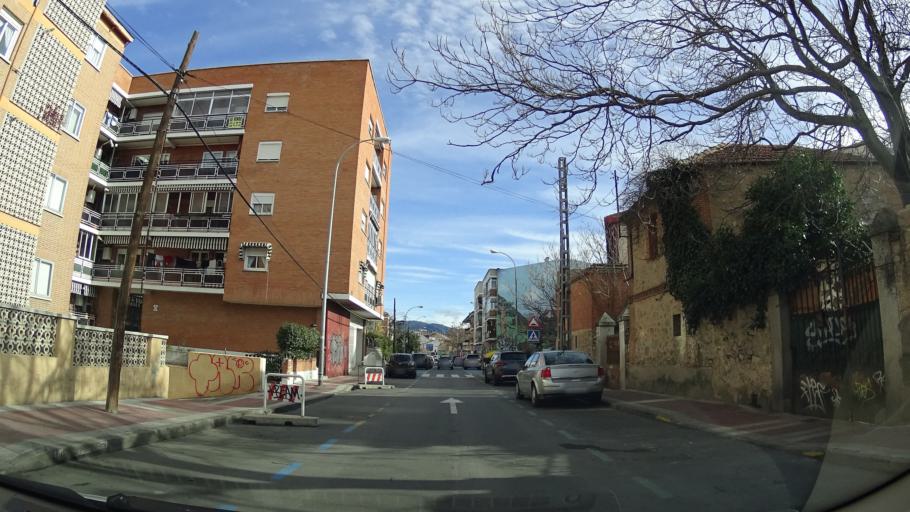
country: ES
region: Madrid
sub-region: Provincia de Madrid
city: Collado-Villalba
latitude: 40.6274
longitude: -4.0125
